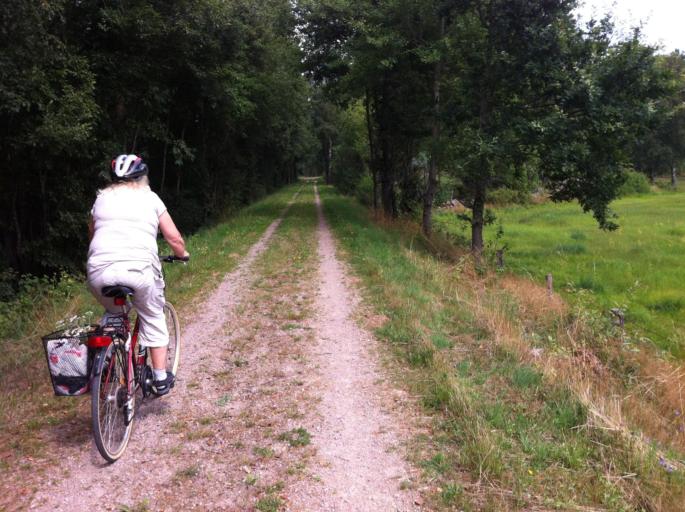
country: SE
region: Skane
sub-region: Horby Kommun
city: Hoerby
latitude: 55.9252
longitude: 13.8090
